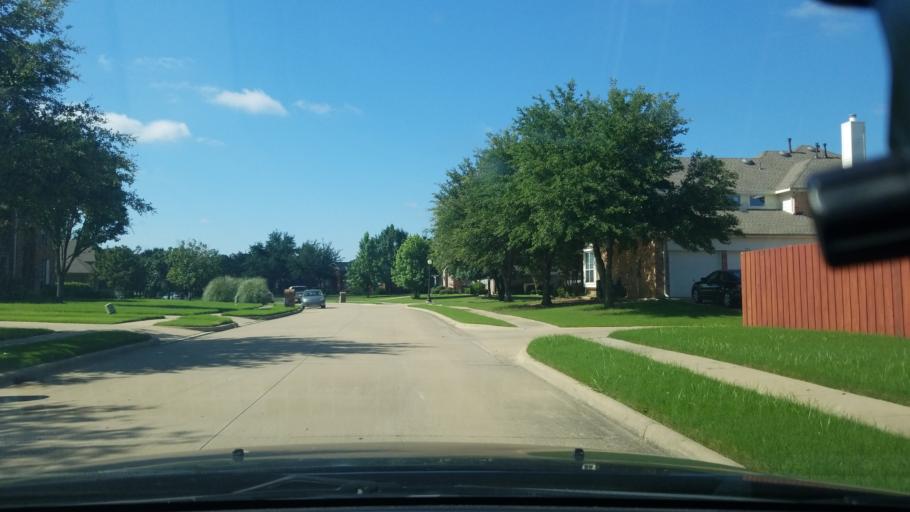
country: US
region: Texas
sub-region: Dallas County
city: Sunnyvale
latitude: 32.8067
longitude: -96.5852
